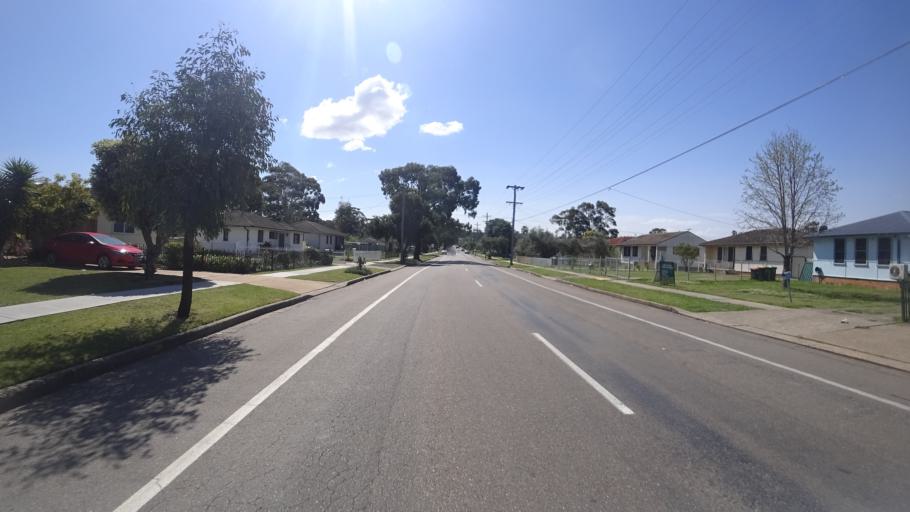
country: AU
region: New South Wales
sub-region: Liverpool
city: Miller
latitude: -33.9186
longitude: 150.8949
